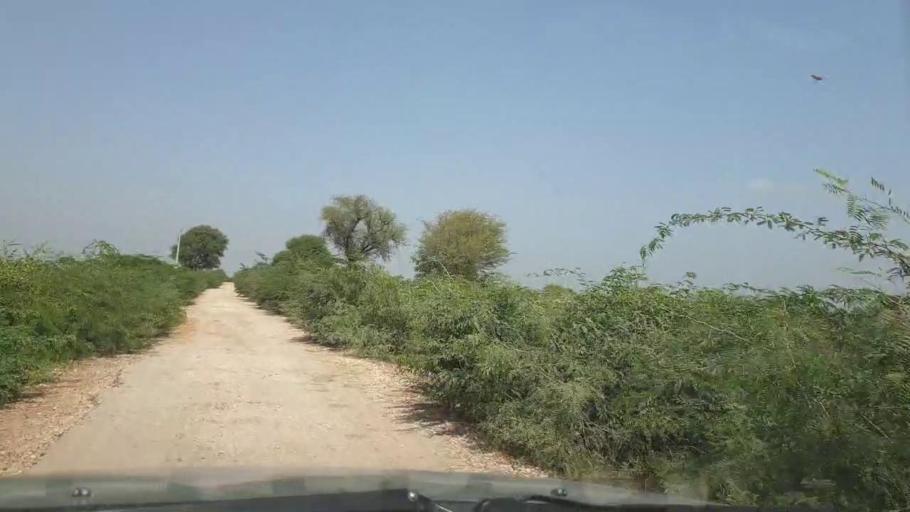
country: PK
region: Sindh
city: Tando Ghulam Ali
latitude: 25.0826
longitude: 68.8020
